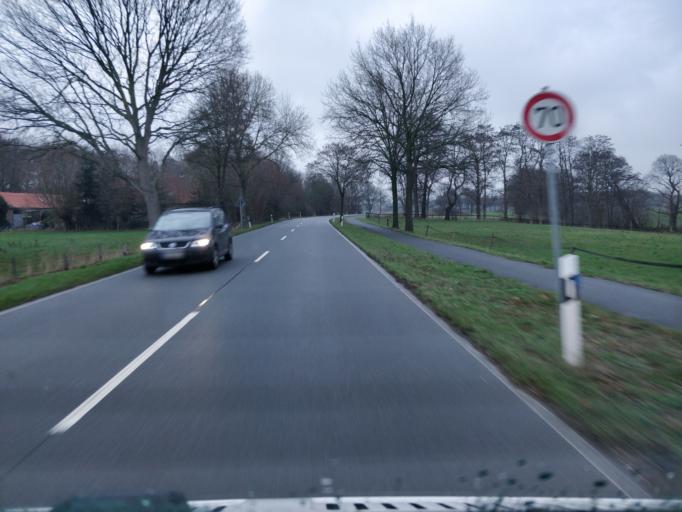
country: DE
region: North Rhine-Westphalia
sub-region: Regierungsbezirk Dusseldorf
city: Mehrhoog
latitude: 51.7590
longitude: 6.5132
